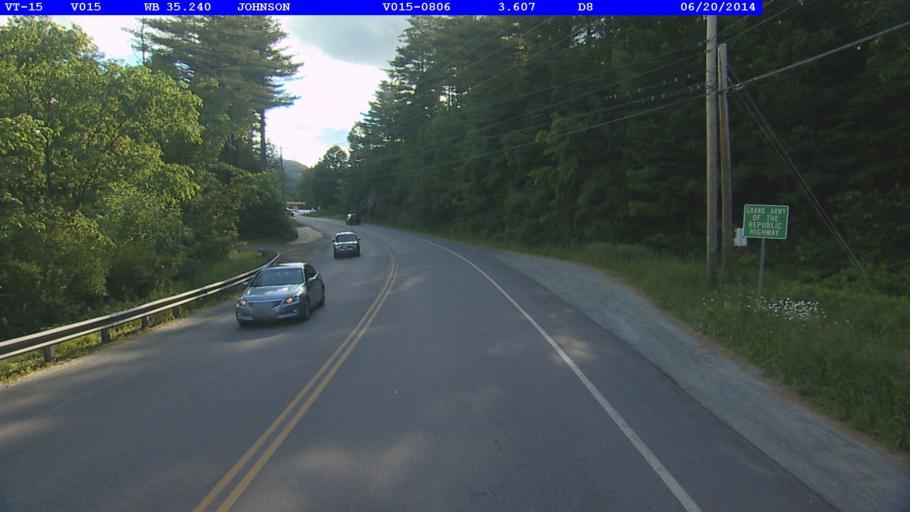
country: US
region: Vermont
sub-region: Lamoille County
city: Johnson
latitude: 44.6363
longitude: -72.6890
